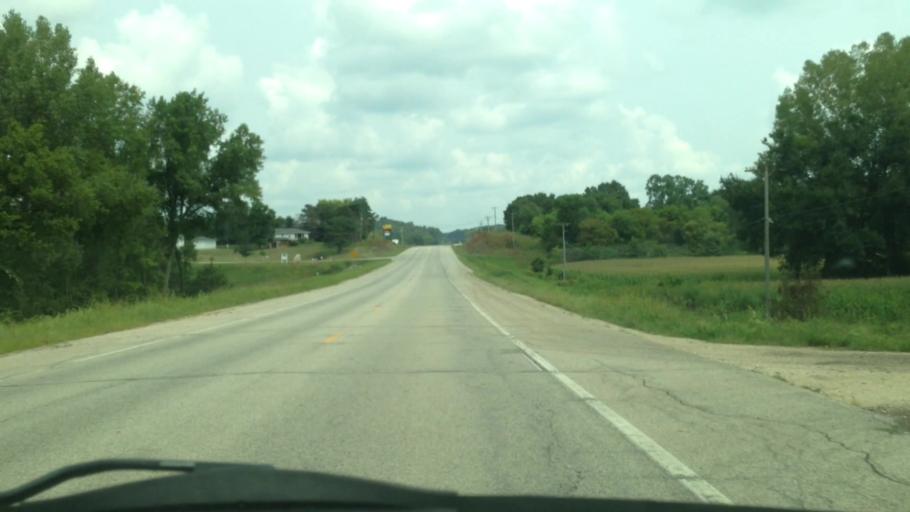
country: US
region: Minnesota
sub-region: Olmsted County
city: Rochester
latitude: 44.0980
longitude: -92.4378
